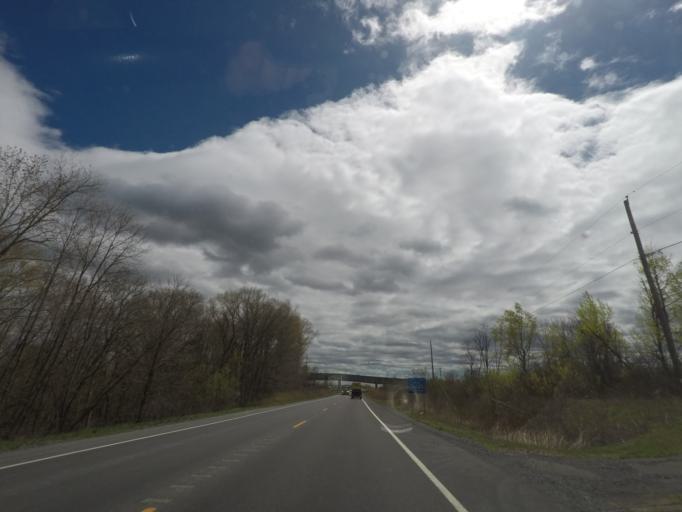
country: US
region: New York
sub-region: Albany County
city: Ravena
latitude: 42.4925
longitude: -73.7936
